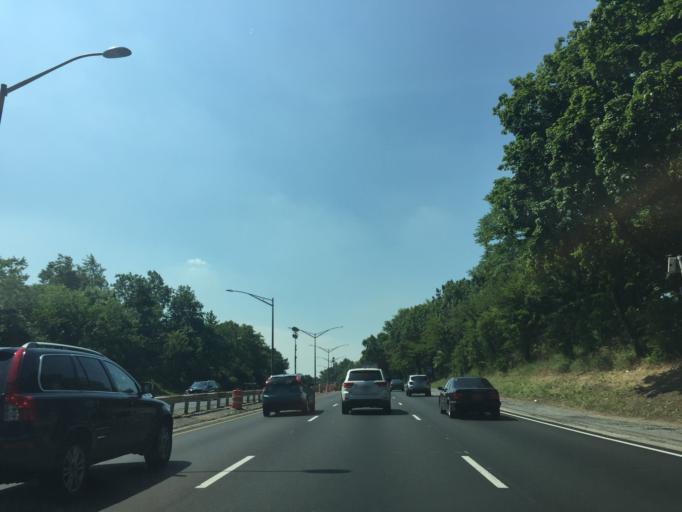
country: US
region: New York
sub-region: Nassau County
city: East Atlantic Beach
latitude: 40.7755
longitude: -73.7845
